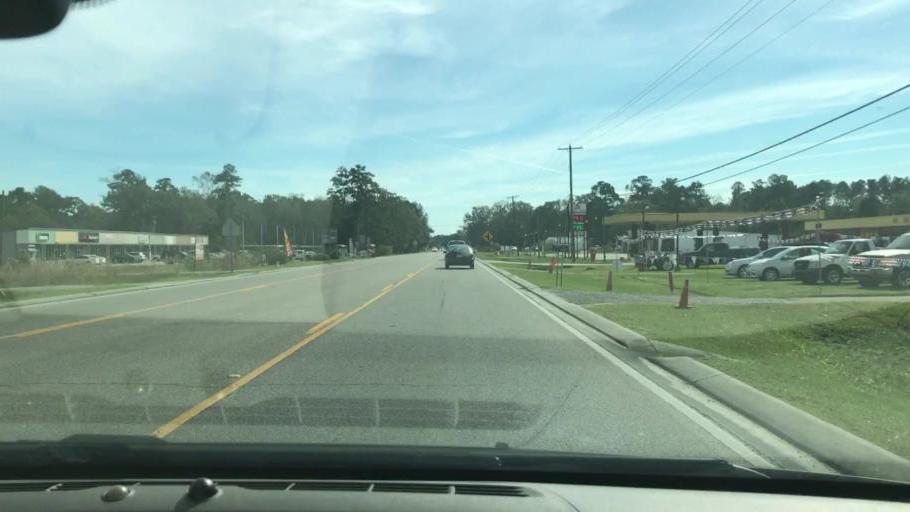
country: US
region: Louisiana
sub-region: Saint Tammany Parish
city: Pearl River
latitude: 30.3674
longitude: -89.7596
